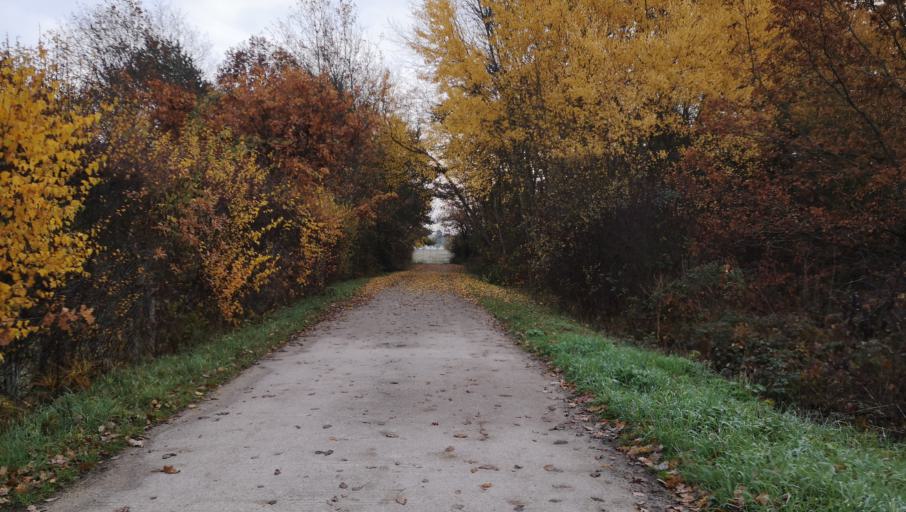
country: FR
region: Centre
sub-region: Departement du Loiret
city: Semoy
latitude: 47.9388
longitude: 1.9567
